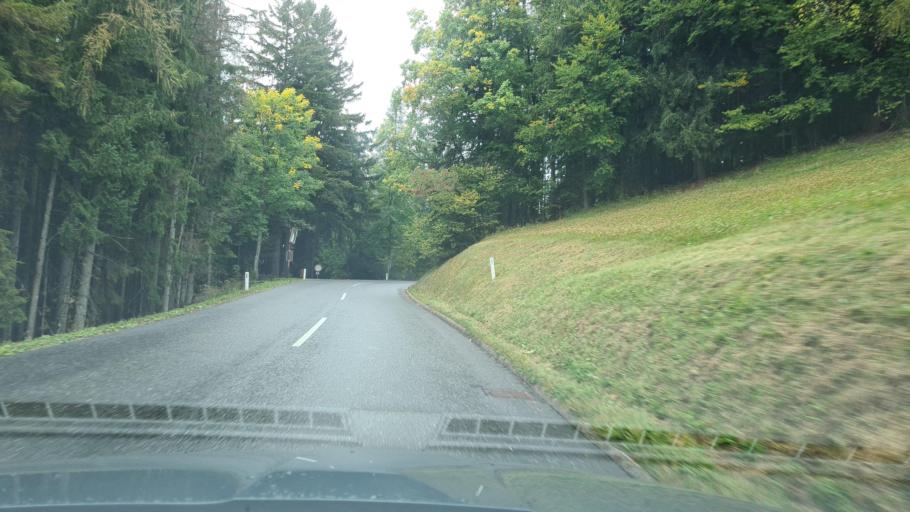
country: AT
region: Styria
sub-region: Politischer Bezirk Weiz
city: Passail
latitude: 47.3217
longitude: 15.4790
